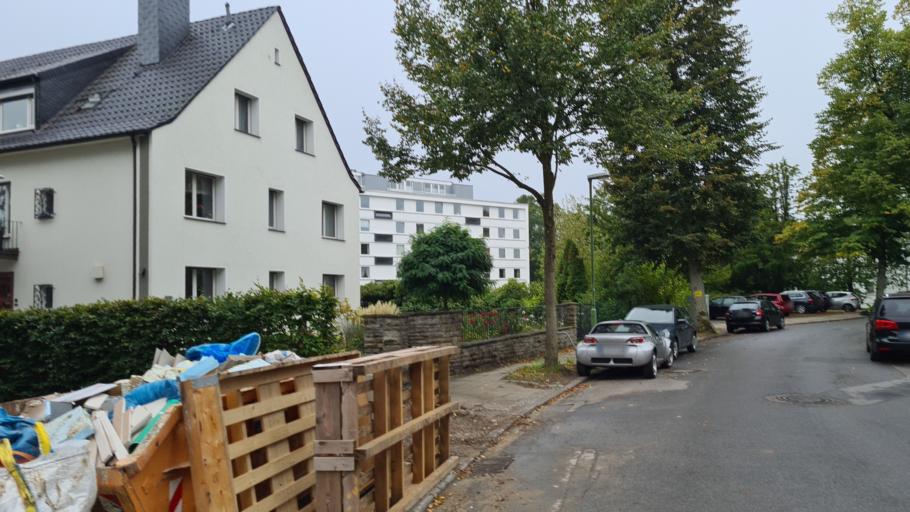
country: DE
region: North Rhine-Westphalia
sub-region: Regierungsbezirk Dusseldorf
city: Essen
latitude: 51.4094
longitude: 6.9971
